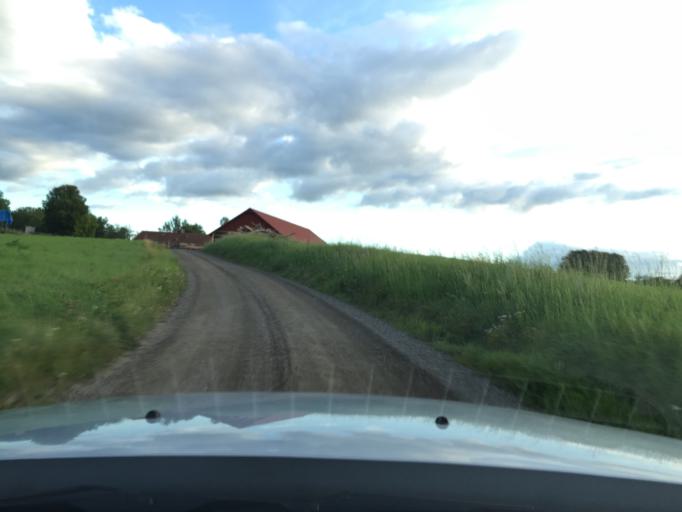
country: SE
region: Skane
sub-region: Hassleholms Kommun
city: Sosdala
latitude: 56.0388
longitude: 13.7093
